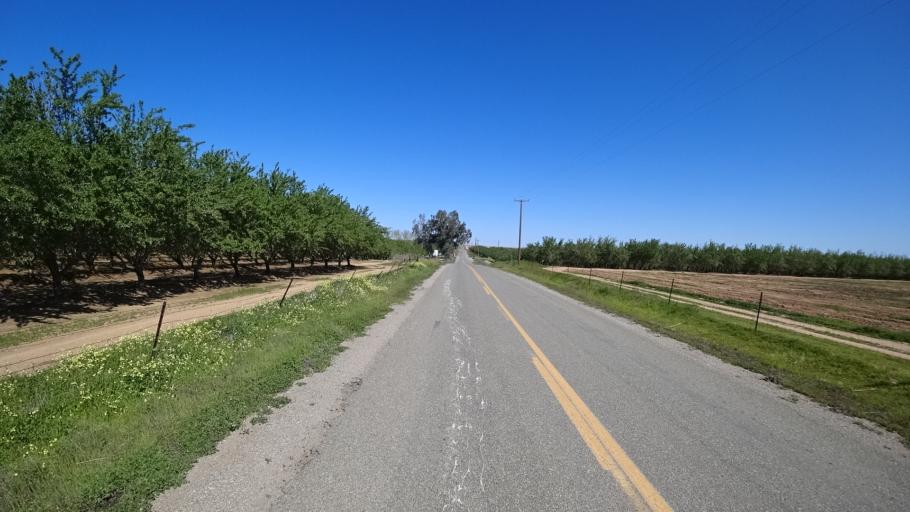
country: US
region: California
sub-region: Glenn County
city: Orland
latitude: 39.6888
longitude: -122.2716
